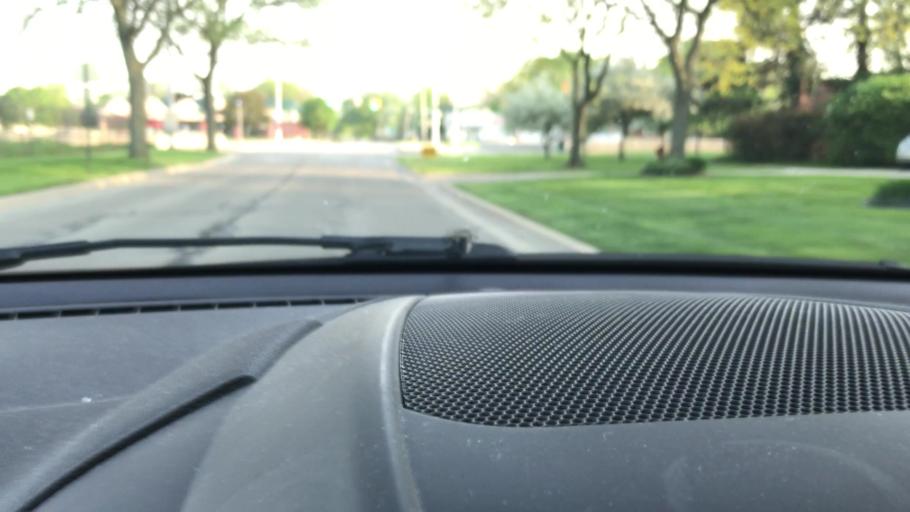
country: US
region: Michigan
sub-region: Oakland County
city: Huntington Woods
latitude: 42.4756
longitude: -83.1729
